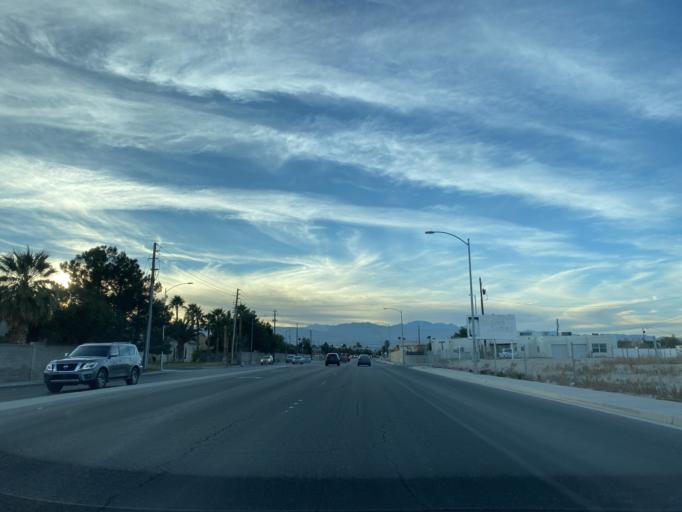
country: US
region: Nevada
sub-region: Clark County
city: Las Vegas
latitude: 36.2611
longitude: -115.2224
